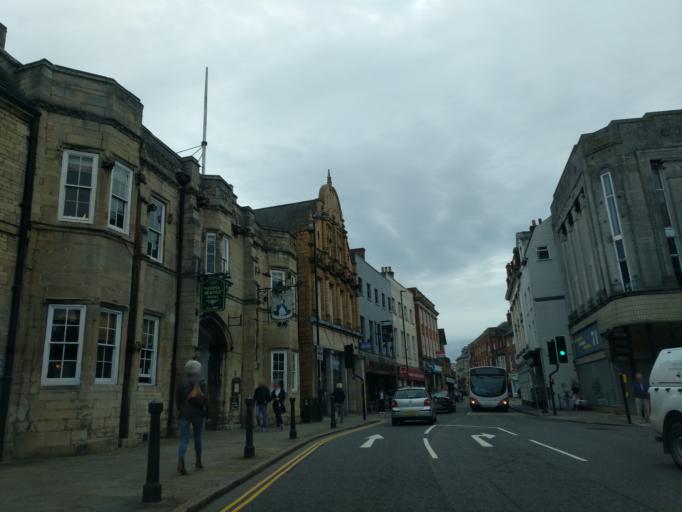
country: GB
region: England
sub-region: Lincolnshire
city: Grantham
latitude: 52.9135
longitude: -0.6431
